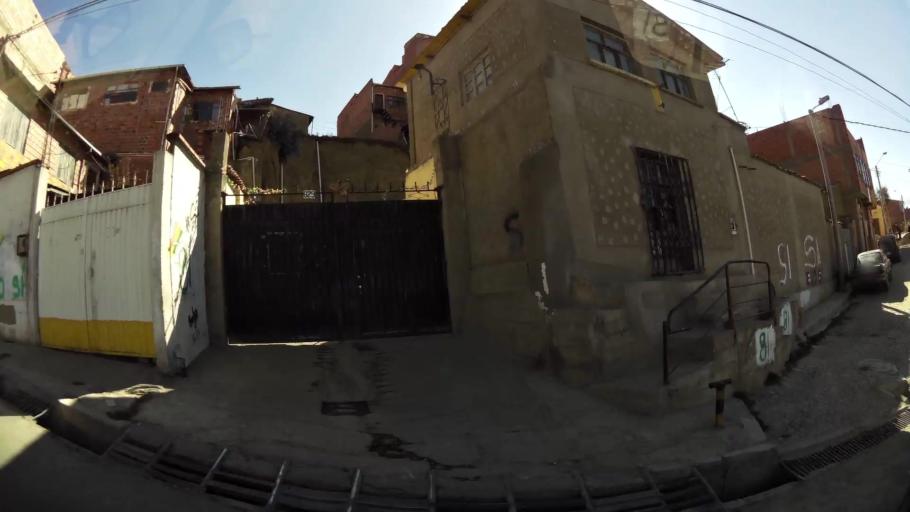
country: BO
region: La Paz
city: La Paz
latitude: -16.5223
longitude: -68.1427
